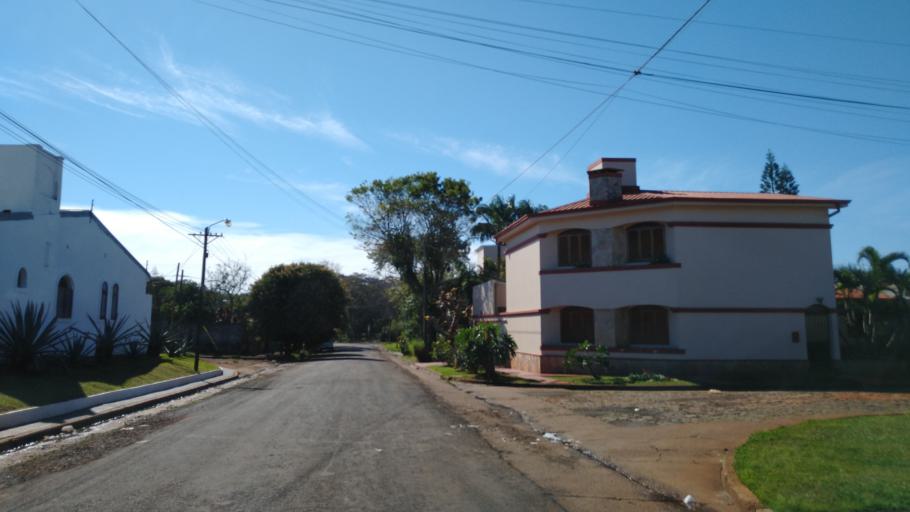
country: AR
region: Misiones
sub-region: Departamento de Capital
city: Posadas
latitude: -27.3646
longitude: -55.9370
